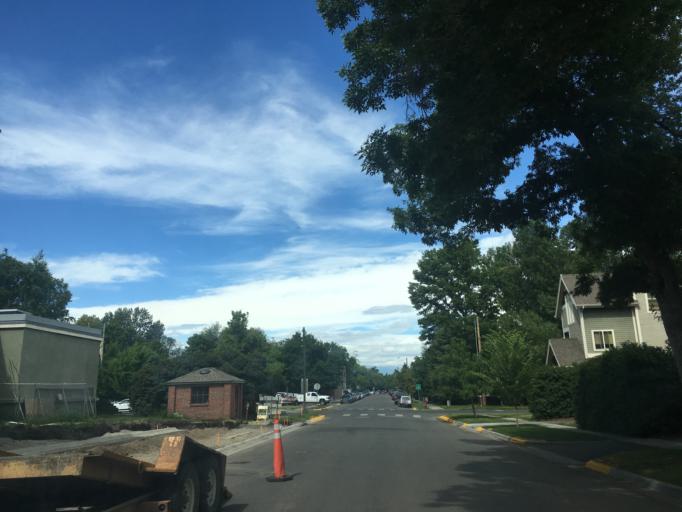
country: US
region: Montana
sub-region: Gallatin County
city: Bozeman
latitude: 45.6815
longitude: -111.0311
